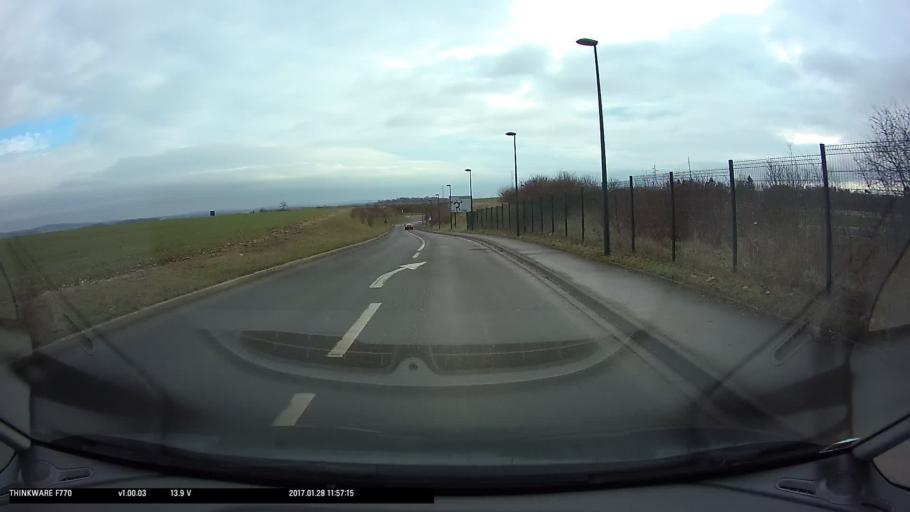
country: FR
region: Ile-de-France
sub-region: Departement du Val-d'Oise
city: Vigny
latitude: 49.0841
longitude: 1.9290
